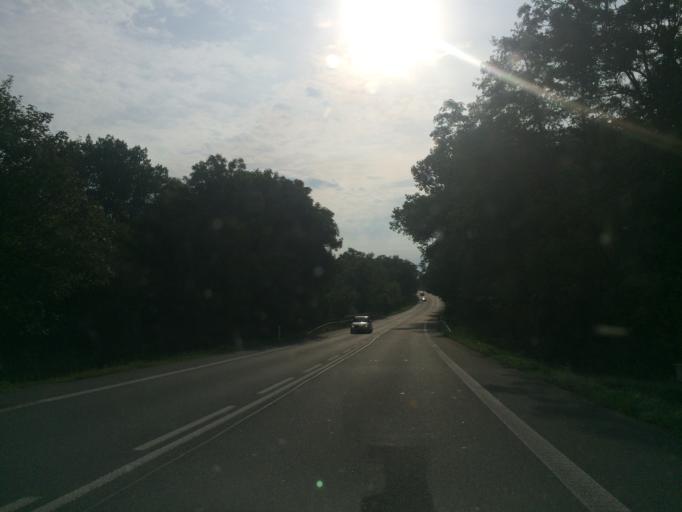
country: CZ
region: Central Bohemia
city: Cesky Brod
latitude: 50.0542
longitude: 14.9090
